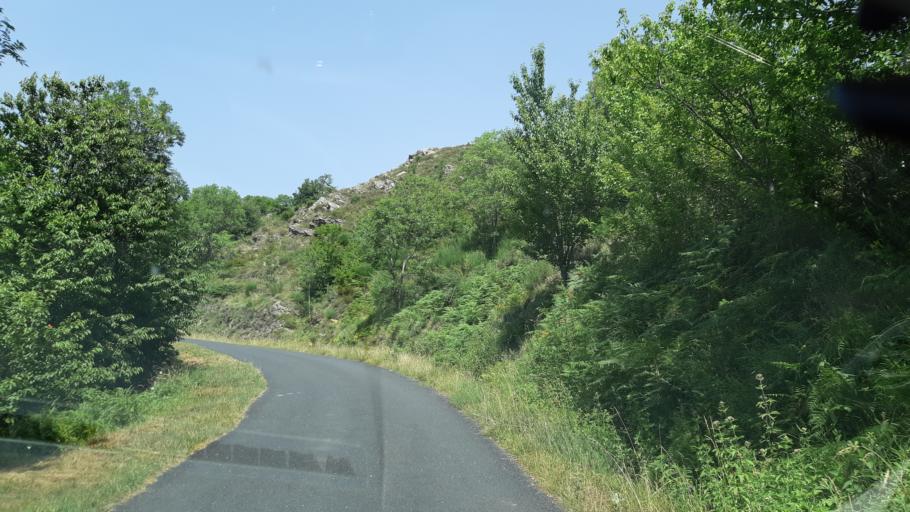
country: FR
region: Languedoc-Roussillon
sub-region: Departement des Pyrenees-Orientales
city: Arles
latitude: 42.5407
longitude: 2.5757
